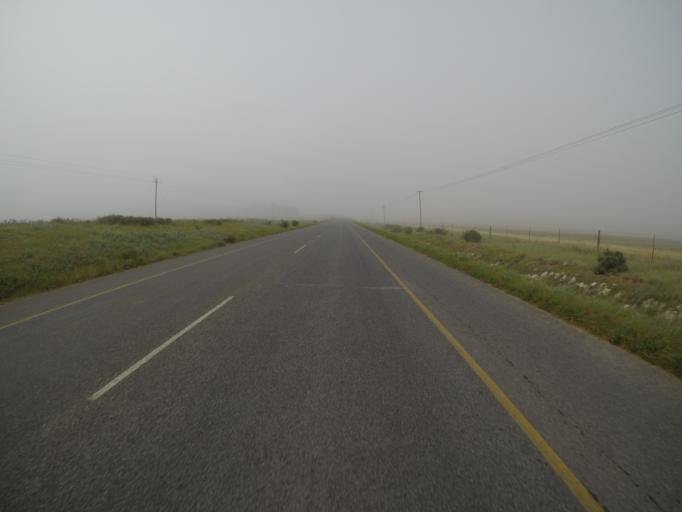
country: ZA
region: Western Cape
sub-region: City of Cape Town
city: Kraaifontein
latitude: -33.6859
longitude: 18.7049
